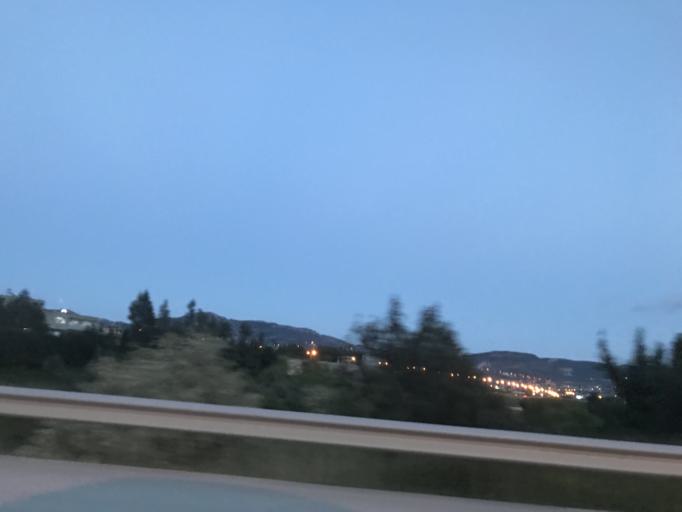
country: TR
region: Hatay
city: Asagiokcular
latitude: 36.1809
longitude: 36.1177
